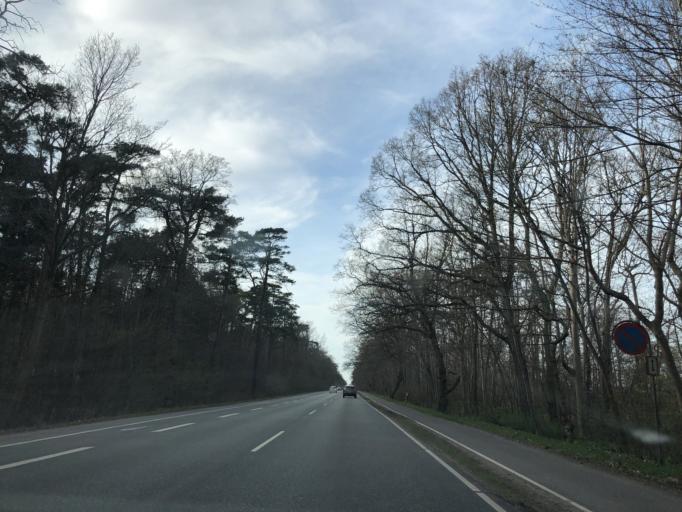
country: DK
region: Zealand
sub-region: Koge Kommune
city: Koge
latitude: 55.4386
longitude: 12.2015
